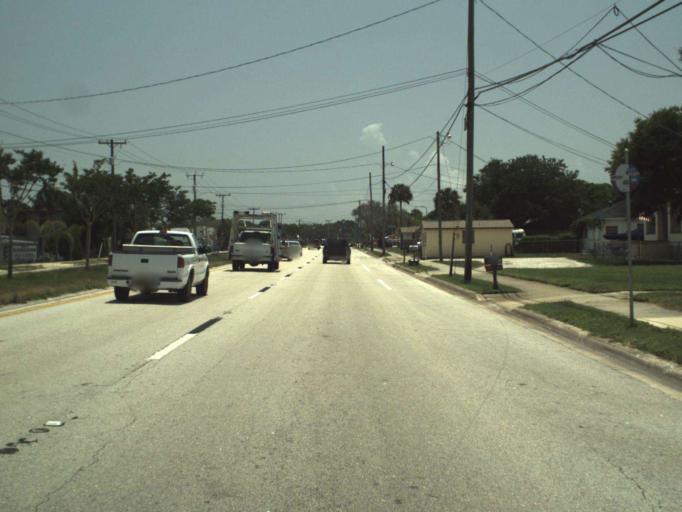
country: US
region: Florida
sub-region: Volusia County
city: Port Orange
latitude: 29.1247
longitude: -80.9782
